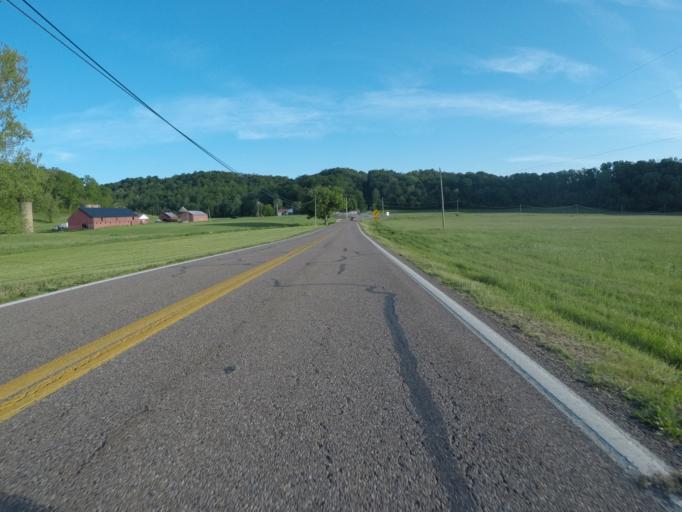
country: US
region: West Virginia
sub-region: Cabell County
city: Huntington
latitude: 38.5254
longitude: -82.4597
